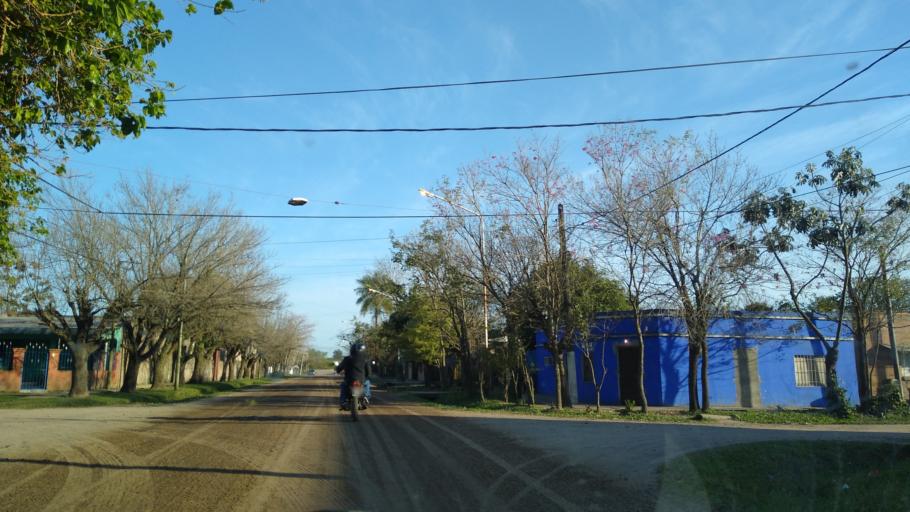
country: AR
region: Chaco
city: Barranqueras
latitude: -27.4713
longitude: -58.9333
